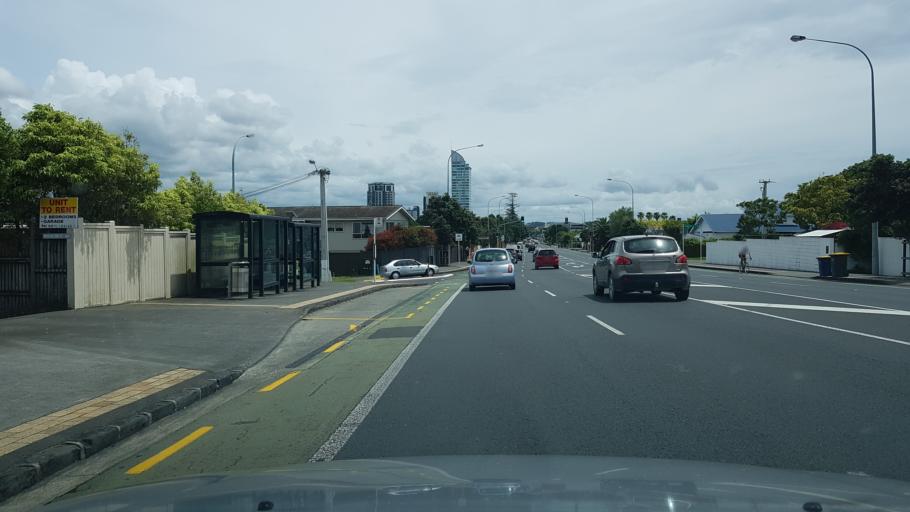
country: NZ
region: Auckland
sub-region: Auckland
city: North Shore
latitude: -36.7965
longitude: 174.7781
